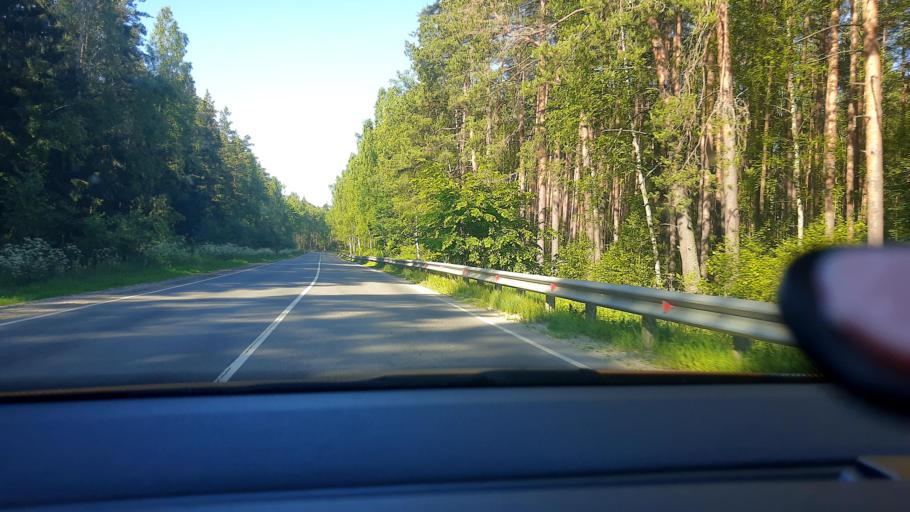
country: RU
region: Moskovskaya
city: Pavlovskiy Posad
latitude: 55.8714
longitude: 38.6889
